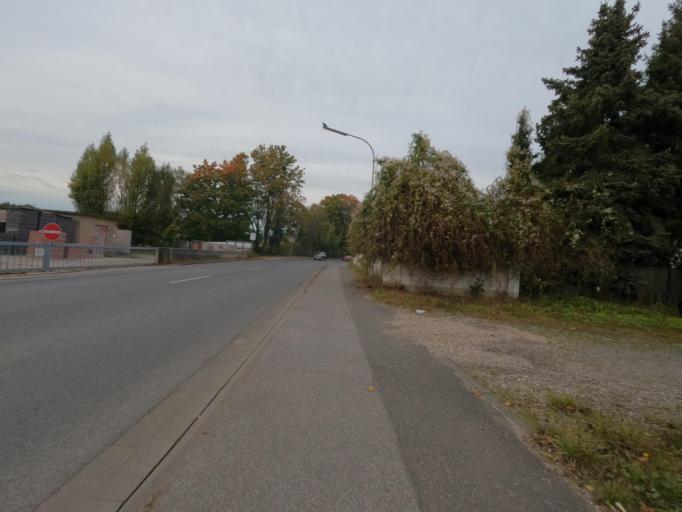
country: DE
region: North Rhine-Westphalia
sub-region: Regierungsbezirk Koln
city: Wassenberg
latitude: 51.0587
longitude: 6.1786
